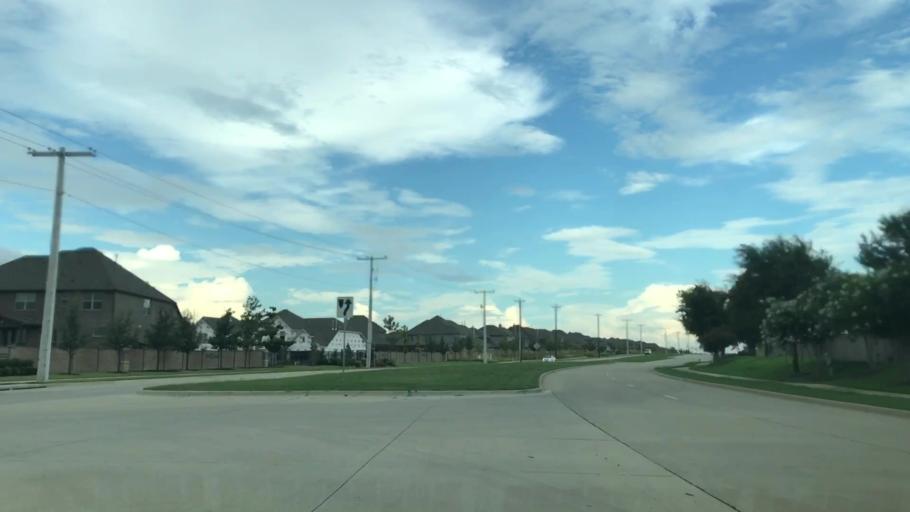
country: US
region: Texas
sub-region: Collin County
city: Prosper
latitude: 33.1889
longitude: -96.7782
